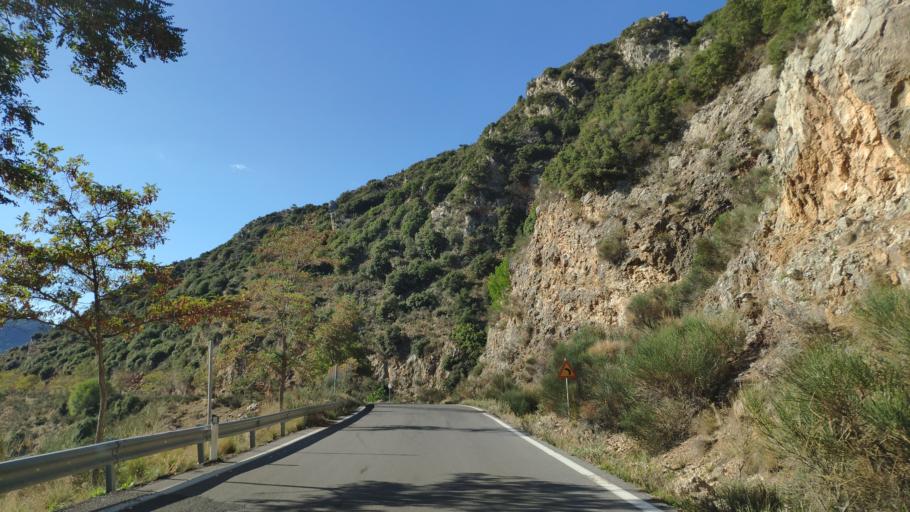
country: GR
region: Peloponnese
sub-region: Nomos Arkadias
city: Dimitsana
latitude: 37.5826
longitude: 22.0554
